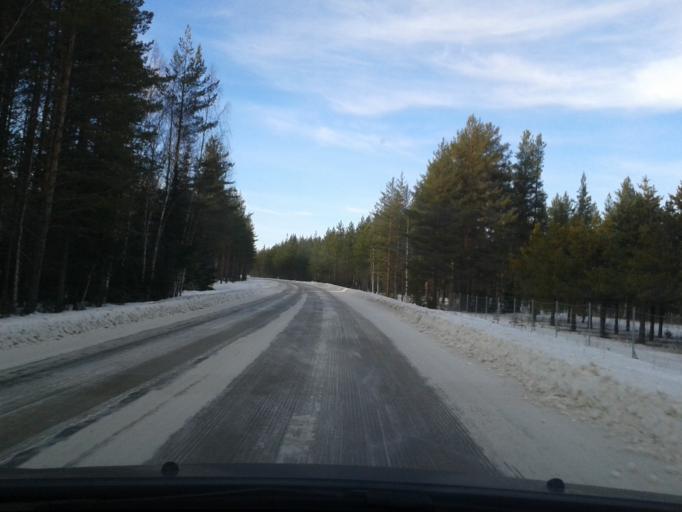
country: SE
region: Vaesternorrland
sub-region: OErnskoeldsviks Kommun
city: Bredbyn
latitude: 63.5574
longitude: 17.9429
